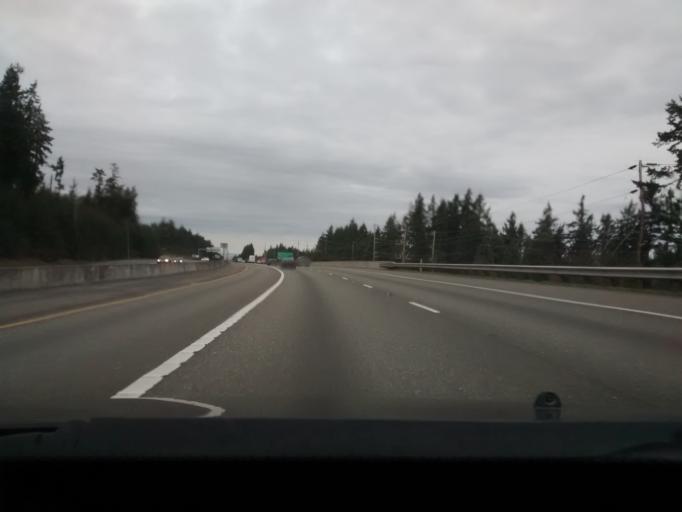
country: US
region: Washington
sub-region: Pierce County
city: Wollochet
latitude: 47.2880
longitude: -122.5612
